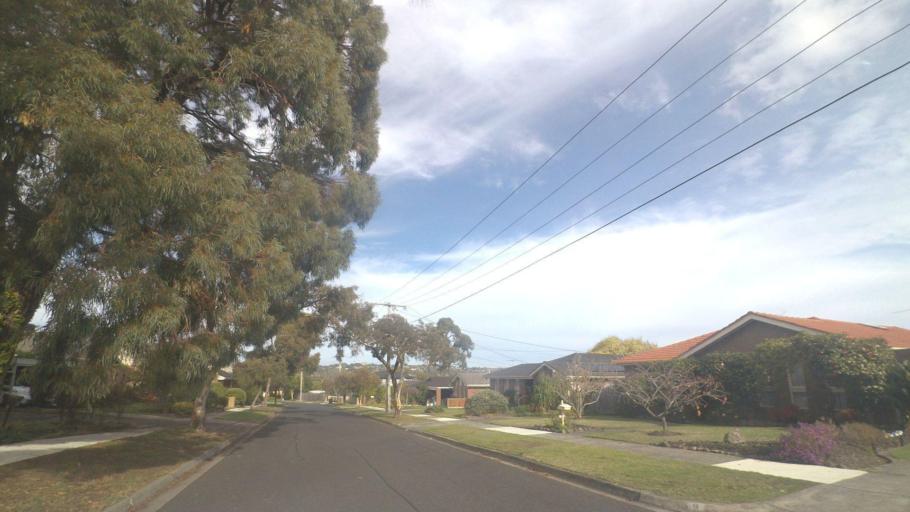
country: AU
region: Victoria
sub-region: Whitehorse
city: Vermont South
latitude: -37.8671
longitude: 145.1841
